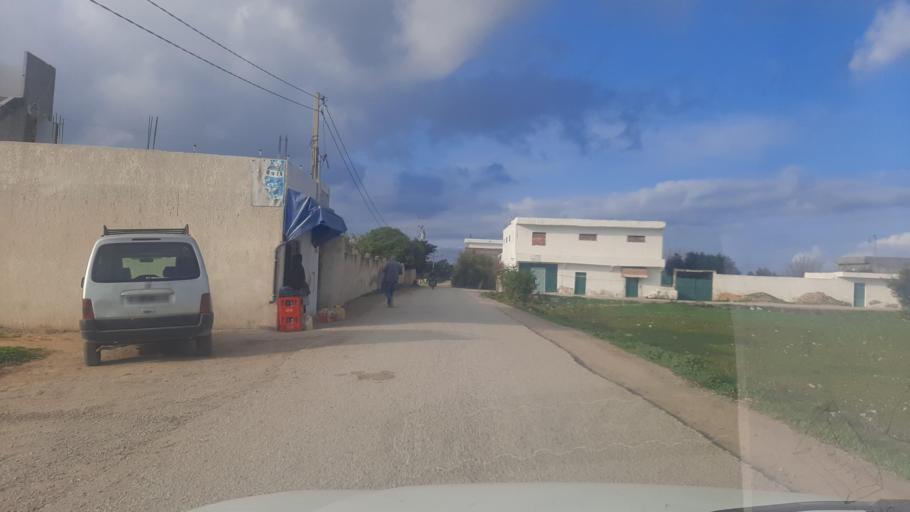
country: TN
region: Nabul
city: Manzil Bu Zalafah
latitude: 36.7158
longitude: 10.4970
